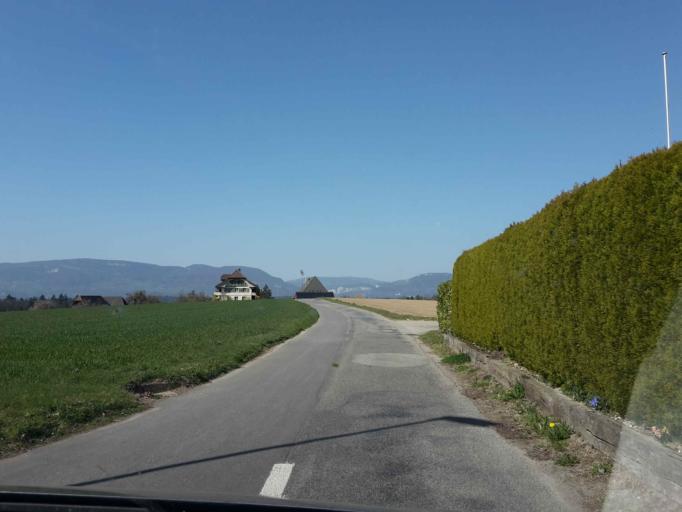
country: CH
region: Bern
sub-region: Oberaargau
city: Herzogenbuchsee
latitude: 47.1962
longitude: 7.7396
